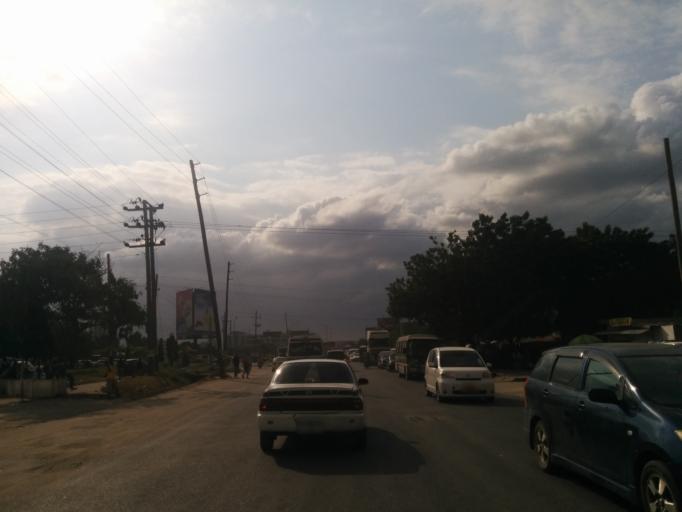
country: TZ
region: Dar es Salaam
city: Dar es Salaam
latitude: -6.8332
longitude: 39.2692
